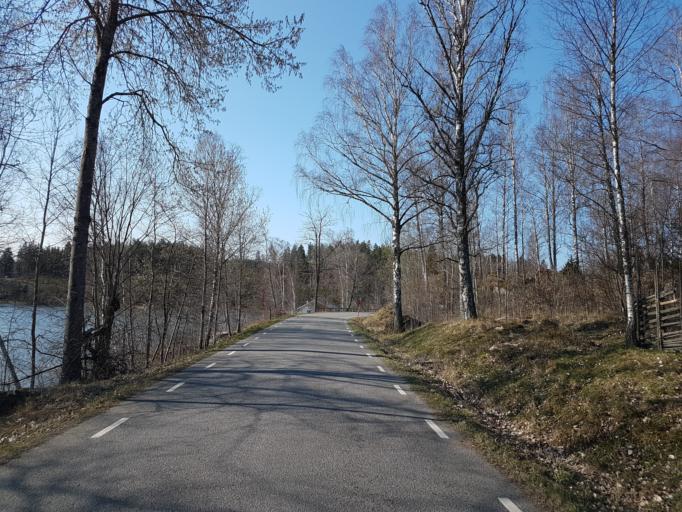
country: SE
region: OEstergoetland
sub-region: Valdemarsviks Kommun
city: Gusum
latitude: 58.1929
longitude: 16.3157
